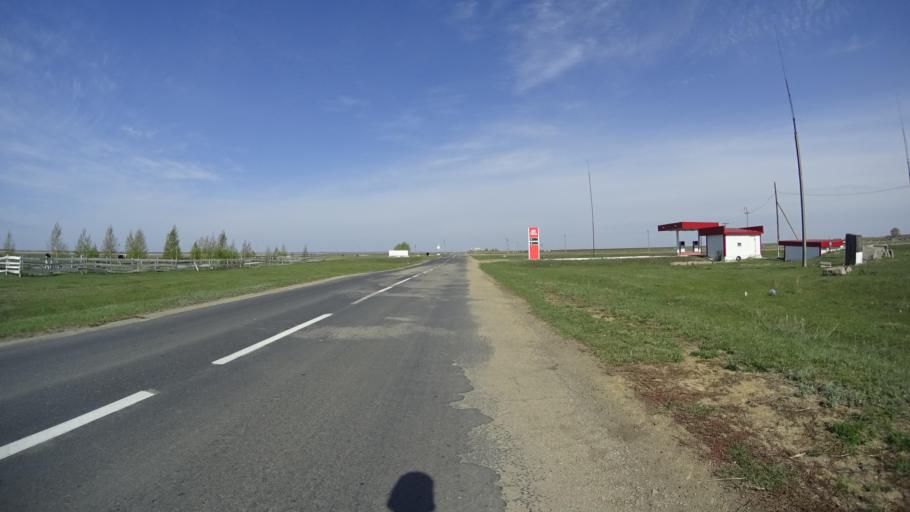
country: RU
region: Chelyabinsk
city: Chesma
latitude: 53.8019
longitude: 61.0160
